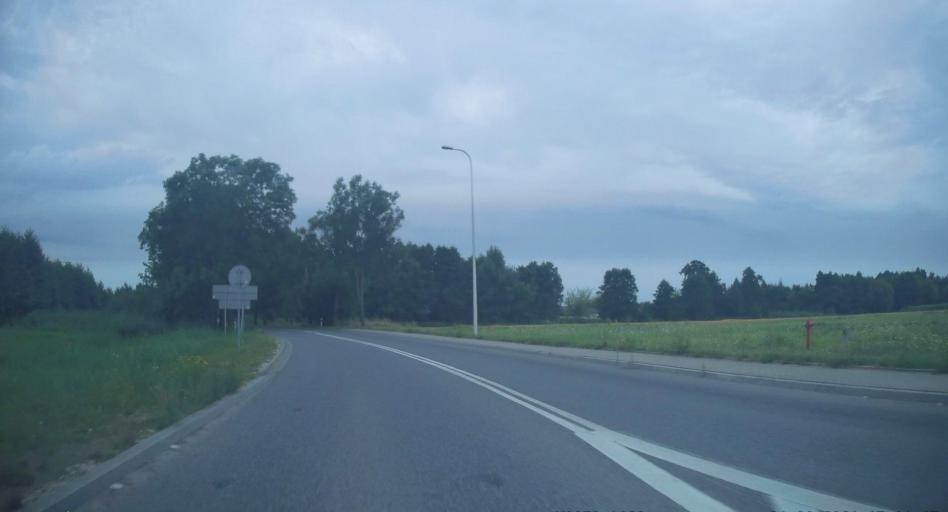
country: PL
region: Lesser Poland Voivodeship
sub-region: Powiat tarnowski
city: Wierzchoslawice
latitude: 50.0113
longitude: 20.8663
